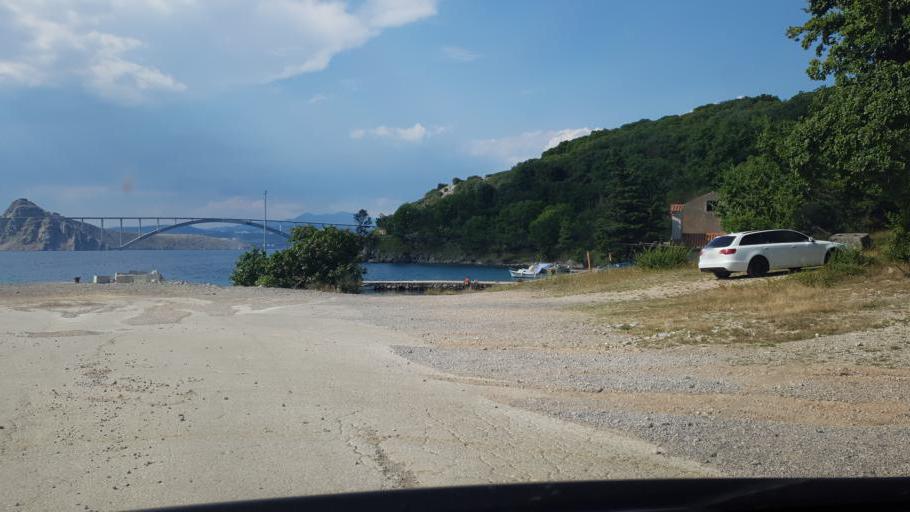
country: HR
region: Primorsko-Goranska
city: Omisalj
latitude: 45.2345
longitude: 14.5793
